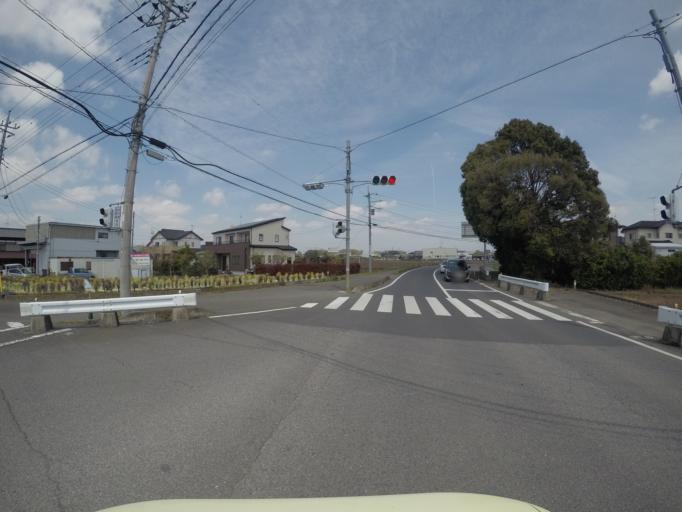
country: JP
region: Ibaraki
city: Shimodate
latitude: 36.3191
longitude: 140.0129
